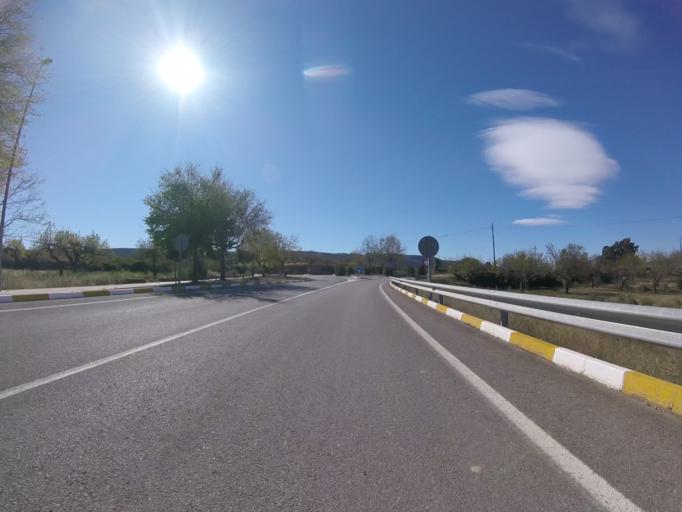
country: ES
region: Valencia
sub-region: Provincia de Castello
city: Albocasser
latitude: 40.3625
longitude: 0.0219
